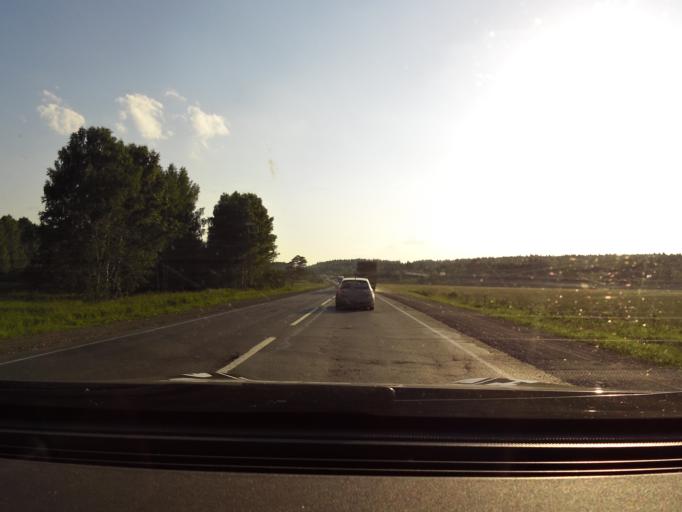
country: RU
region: Sverdlovsk
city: Druzhinino
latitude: 56.8103
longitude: 59.5054
